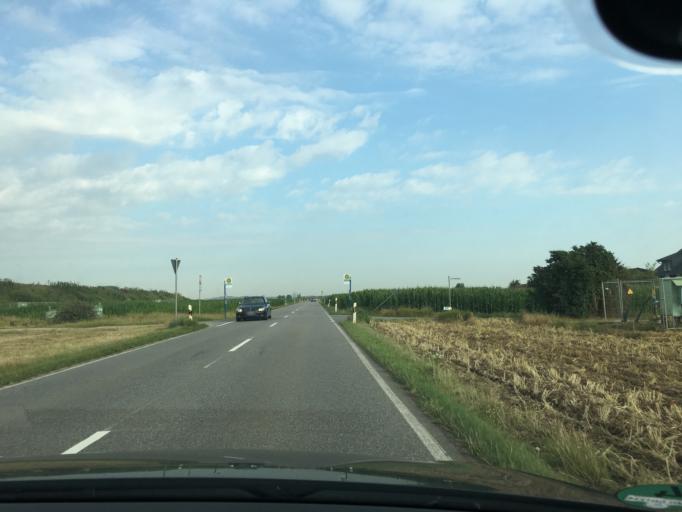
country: DE
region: North Rhine-Westphalia
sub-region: Regierungsbezirk Koln
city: Niederzier
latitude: 50.8567
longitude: 6.4225
